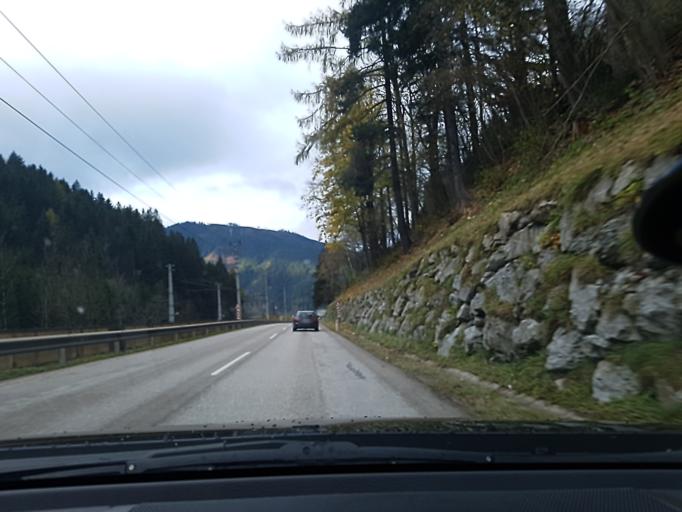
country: AT
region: Styria
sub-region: Politischer Bezirk Liezen
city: Selzthal
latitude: 47.5408
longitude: 14.3079
